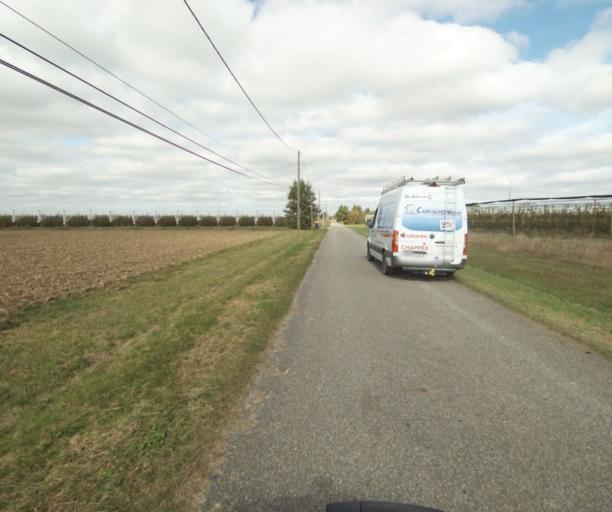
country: FR
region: Midi-Pyrenees
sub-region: Departement du Tarn-et-Garonne
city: Finhan
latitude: 43.9380
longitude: 1.2168
